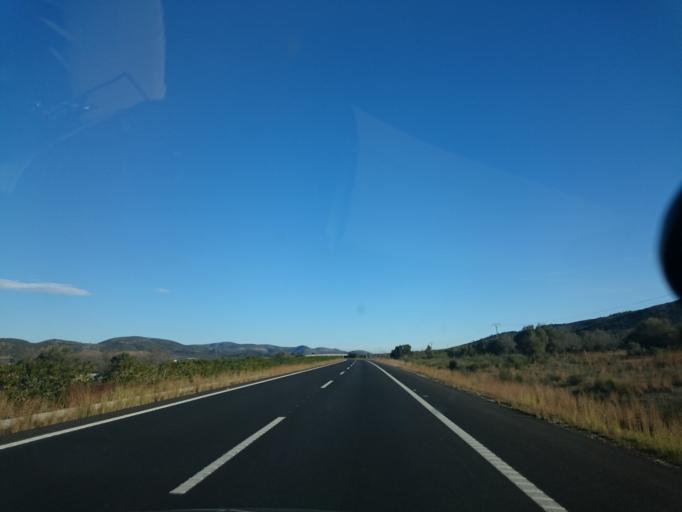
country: ES
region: Valencia
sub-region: Provincia de Castello
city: Alcala de Xivert
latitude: 40.3163
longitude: 0.2480
